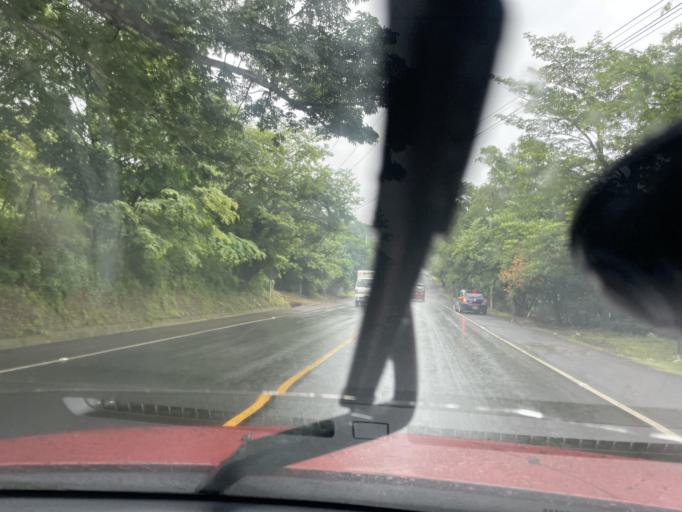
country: SV
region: Morazan
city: Jocoro
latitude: 13.5632
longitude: -88.0988
